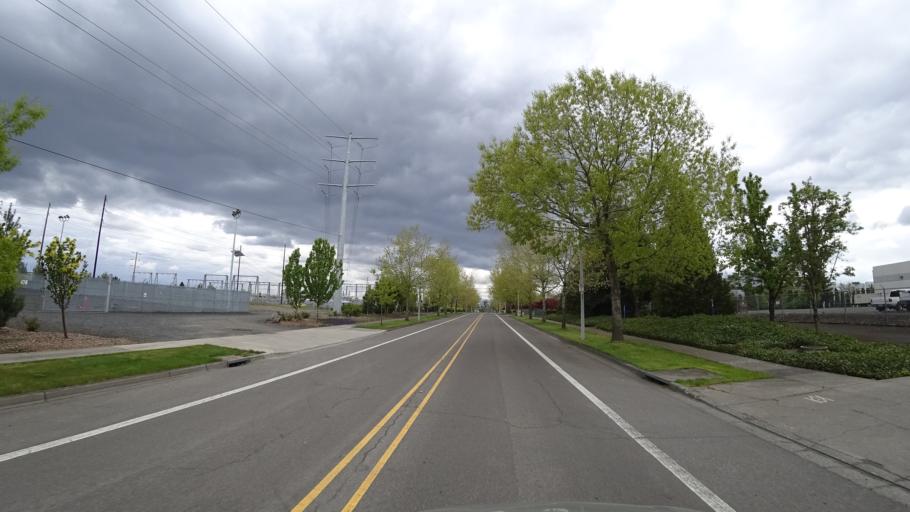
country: US
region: Oregon
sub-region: Washington County
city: Rockcreek
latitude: 45.5537
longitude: -122.9184
